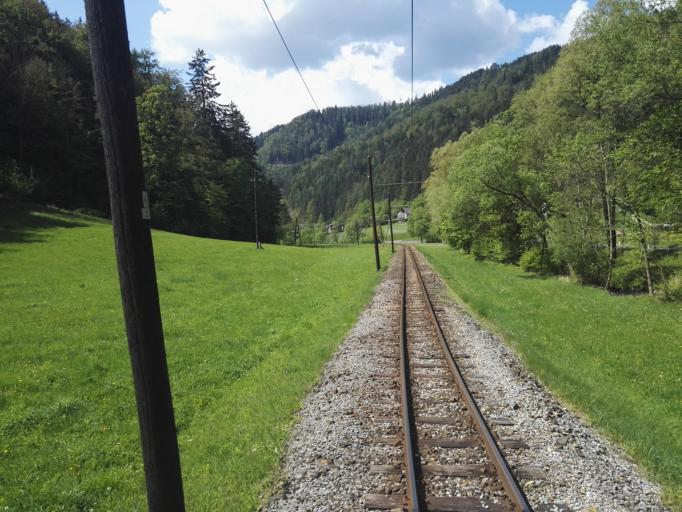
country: AT
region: Styria
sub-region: Politischer Bezirk Bruck-Muerzzuschlag
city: Pernegg an der Mur
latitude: 47.3616
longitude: 15.3753
